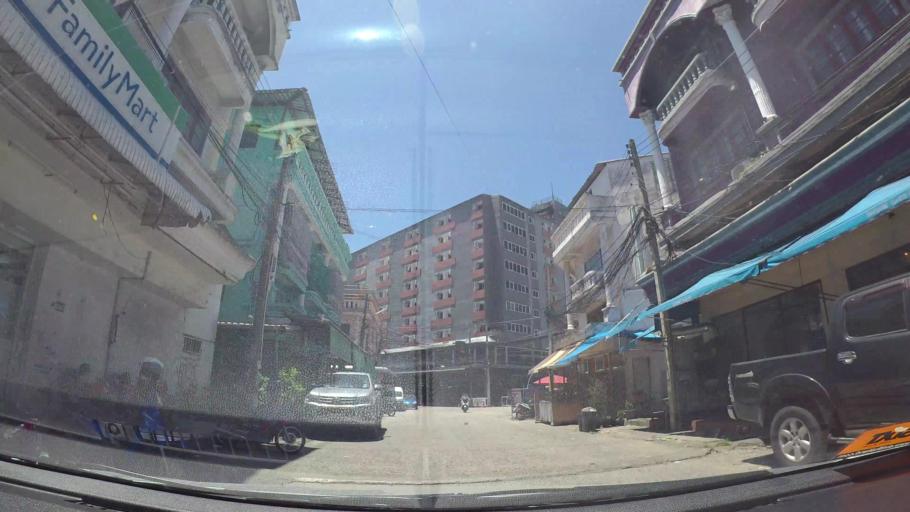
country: TH
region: Chon Buri
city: Phatthaya
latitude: 12.9221
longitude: 100.8785
